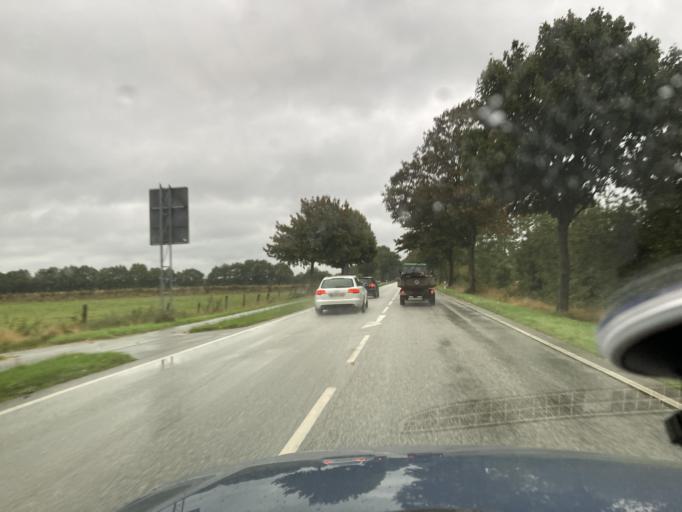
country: DE
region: Schleswig-Holstein
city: Fockbek
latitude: 54.2814
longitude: 9.5745
